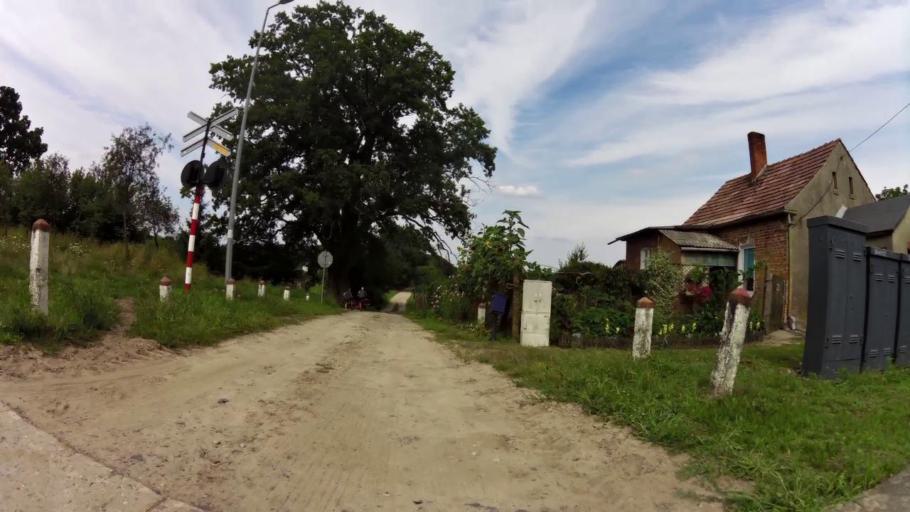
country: PL
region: West Pomeranian Voivodeship
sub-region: Powiat lobeski
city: Wegorzyno
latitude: 53.5333
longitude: 15.6148
